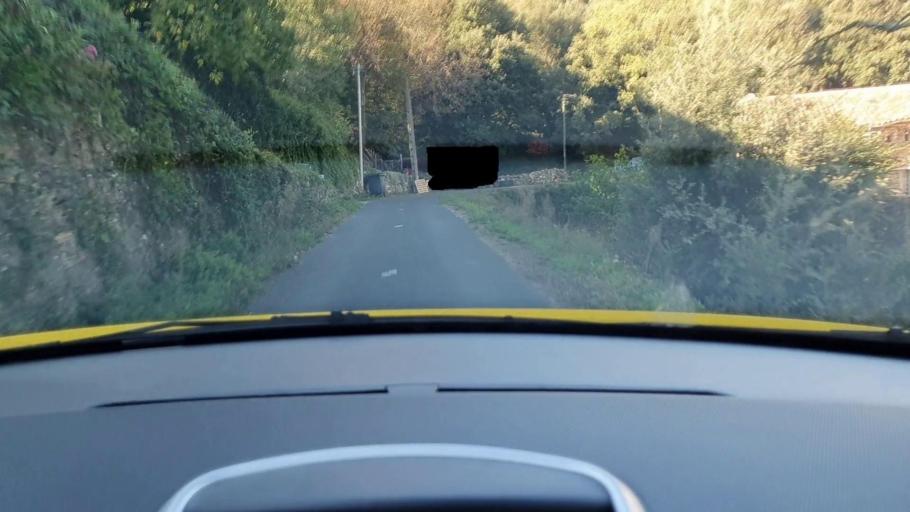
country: FR
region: Languedoc-Roussillon
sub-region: Departement du Gard
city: Sumene
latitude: 44.0247
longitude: 3.7560
